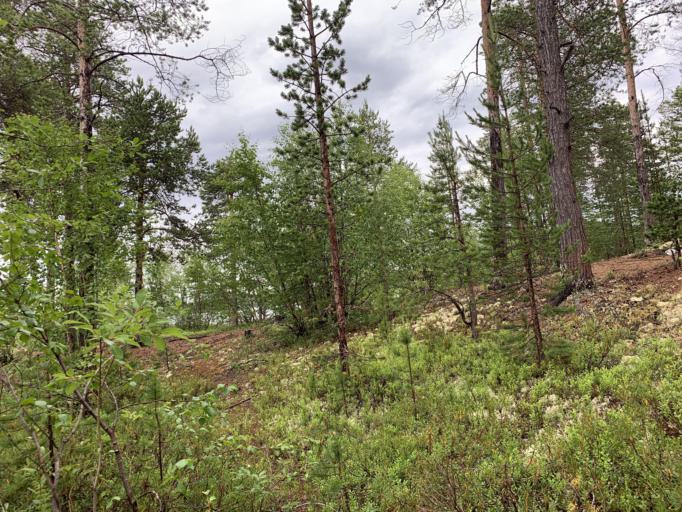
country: RU
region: Murmansk
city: Monchegorsk
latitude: 67.9541
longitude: 33.0257
